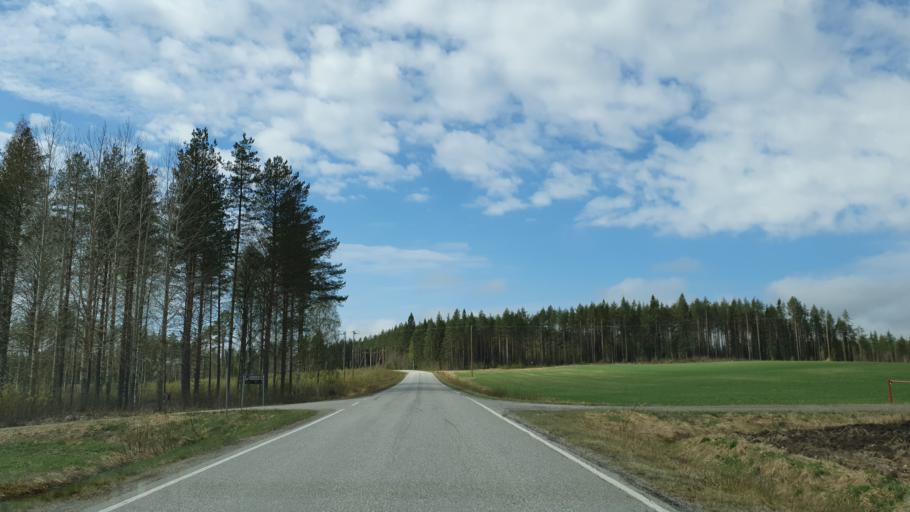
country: FI
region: Kainuu
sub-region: Kehys-Kainuu
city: Kuhmo
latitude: 64.1201
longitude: 29.6902
